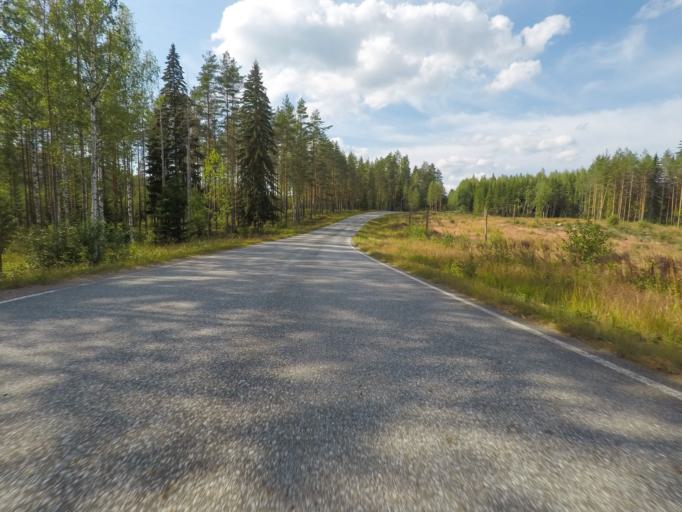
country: FI
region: Southern Savonia
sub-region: Mikkeli
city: Puumala
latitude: 61.6971
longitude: 28.2139
